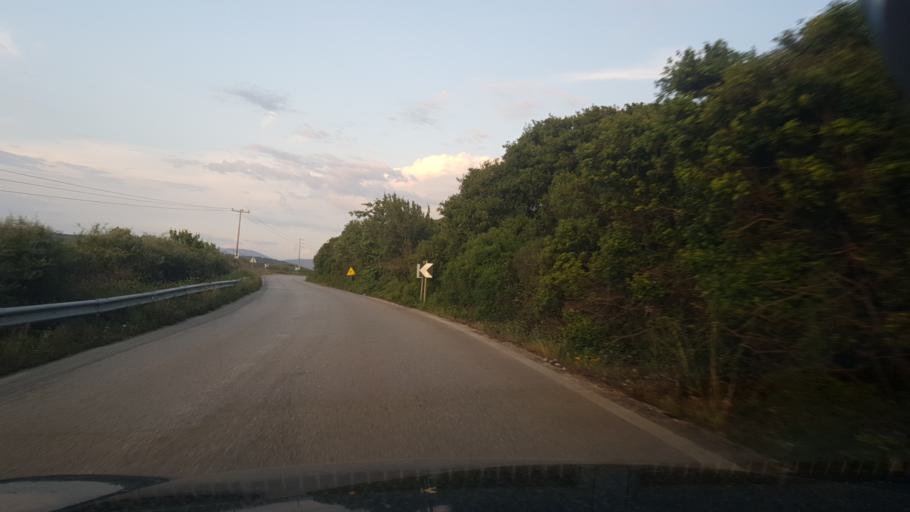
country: GR
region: Ionian Islands
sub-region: Lefkada
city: Lefkada
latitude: 38.8639
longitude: 20.7732
